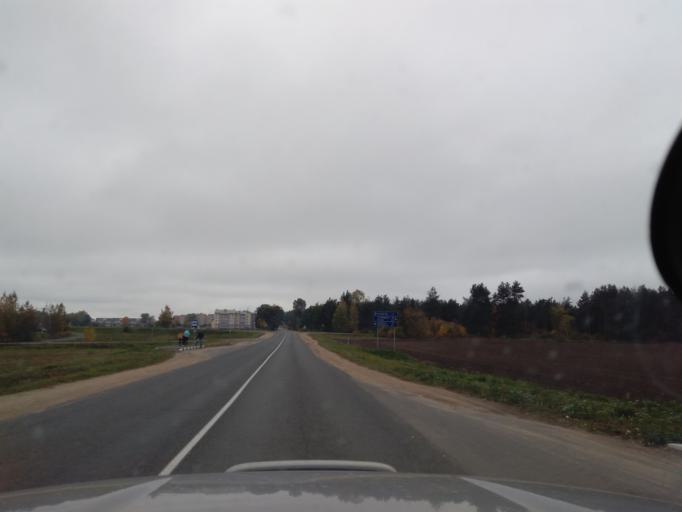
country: BY
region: Minsk
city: Kapyl'
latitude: 53.1497
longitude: 27.1259
